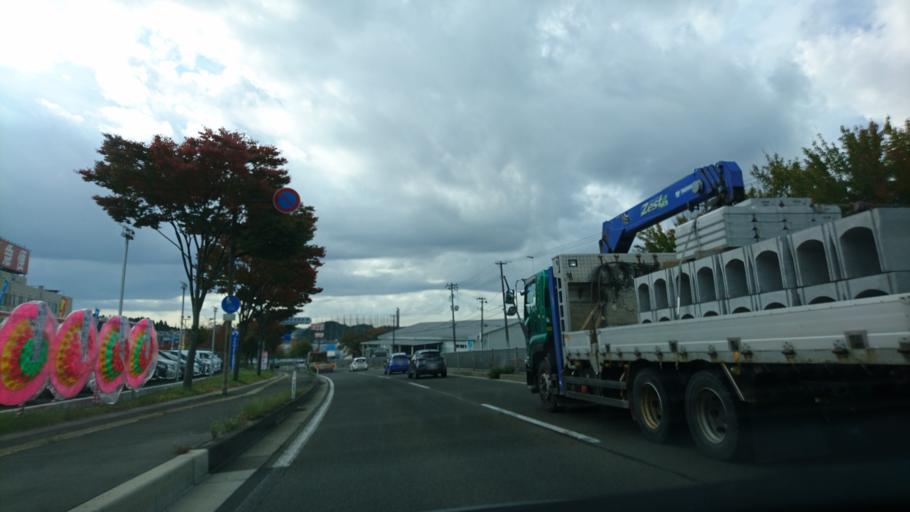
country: JP
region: Miyagi
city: Tomiya
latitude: 38.3564
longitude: 140.8710
